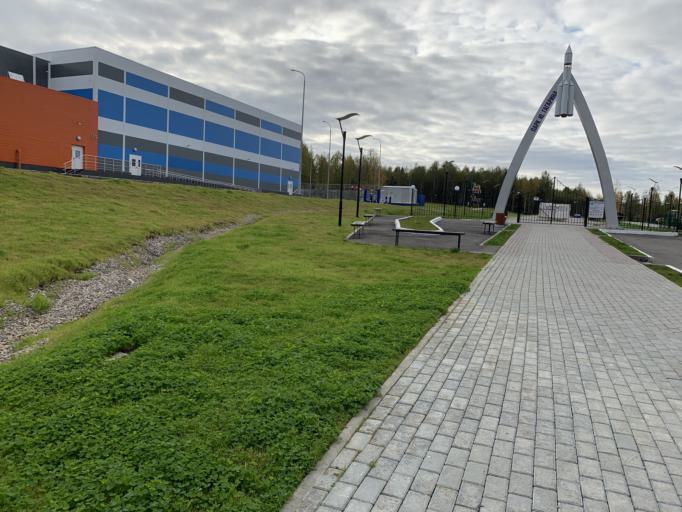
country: RU
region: Perm
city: Gubakha
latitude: 58.8341
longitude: 57.5606
